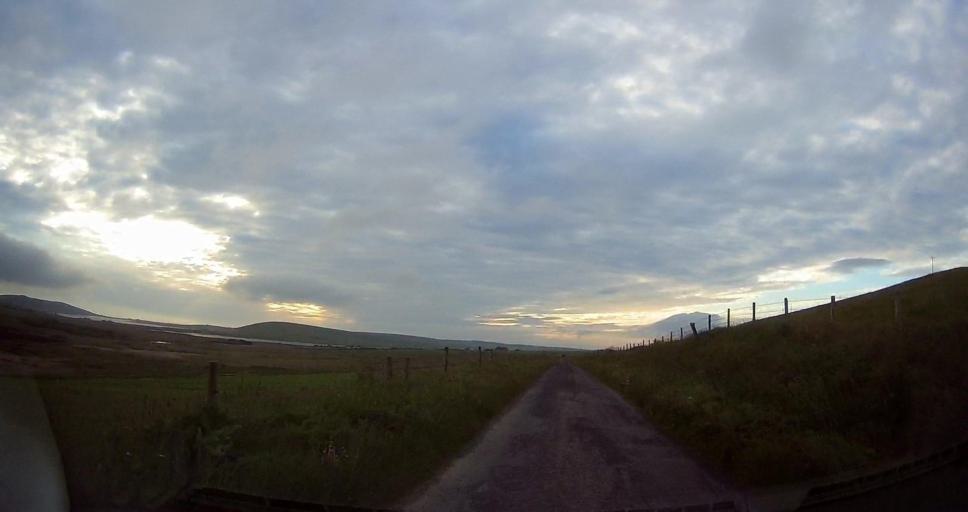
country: GB
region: Scotland
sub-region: Orkney Islands
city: Stromness
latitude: 59.1033
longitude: -3.2117
